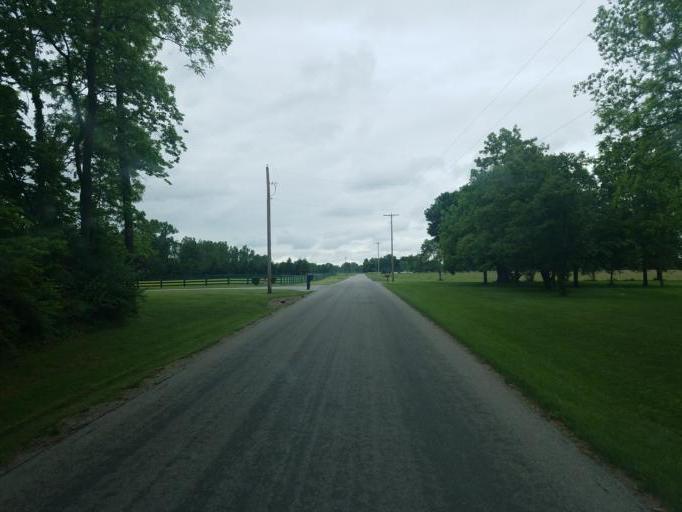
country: US
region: Ohio
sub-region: Morrow County
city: Mount Gilead
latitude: 40.5524
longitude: -82.8719
